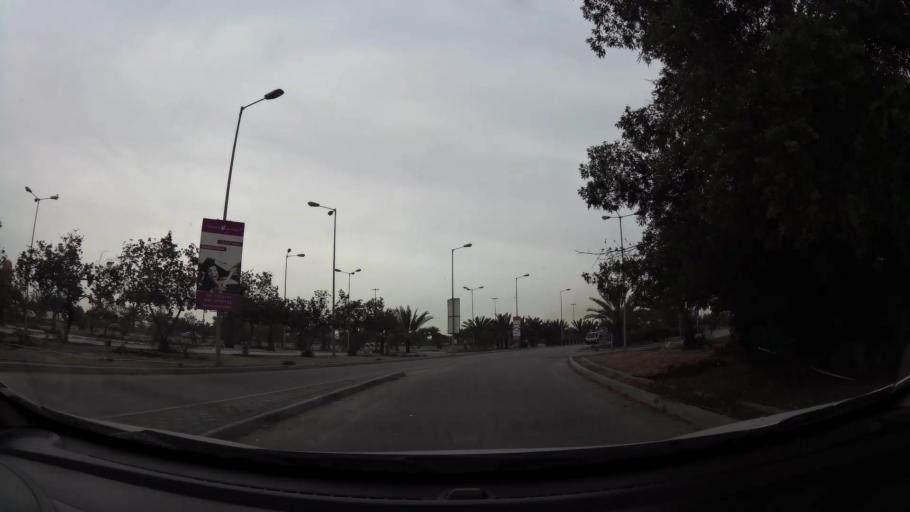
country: BH
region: Manama
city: Jidd Hafs
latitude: 26.1988
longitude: 50.5521
